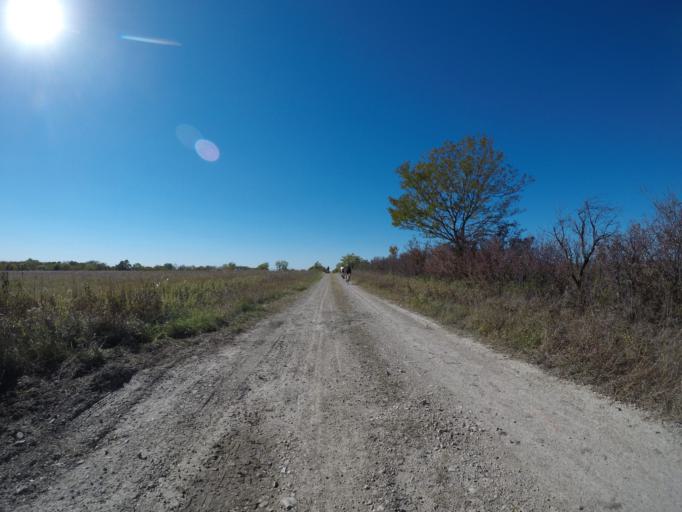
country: US
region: Kansas
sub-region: Wabaunsee County
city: Alma
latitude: 38.9710
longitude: -96.4645
